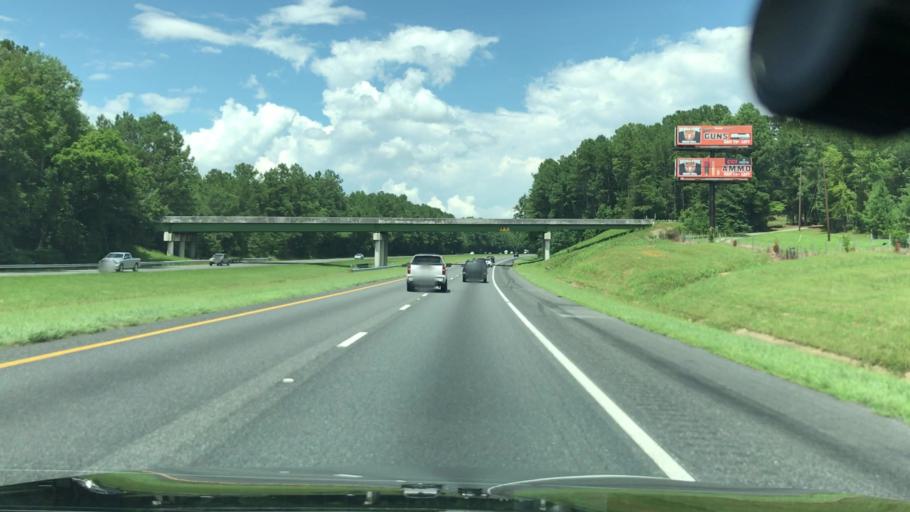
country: US
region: South Carolina
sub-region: York County
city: Rock Hill
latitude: 34.8320
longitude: -81.0300
